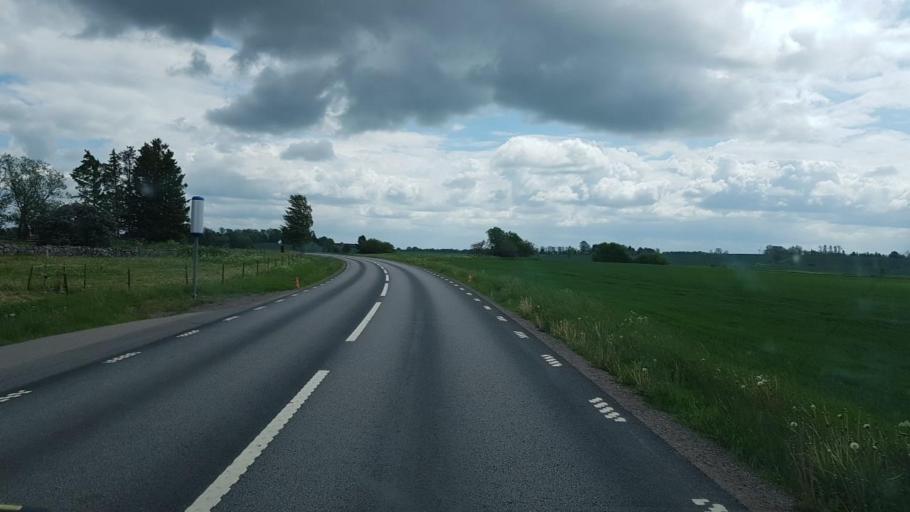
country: SE
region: OEstergoetland
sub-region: Motala Kommun
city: Borensberg
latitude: 58.4821
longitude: 15.2157
